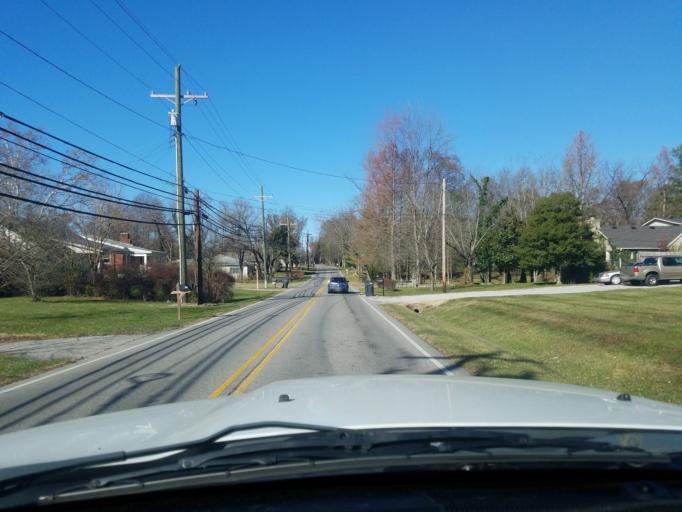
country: US
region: Indiana
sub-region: Floyd County
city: New Albany
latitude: 38.3259
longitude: -85.8020
